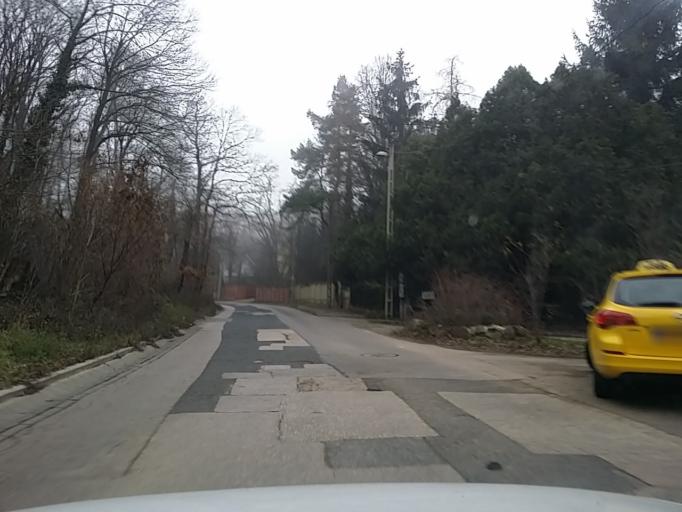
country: HU
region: Pest
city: Budakeszi
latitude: 47.5311
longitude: 18.9473
